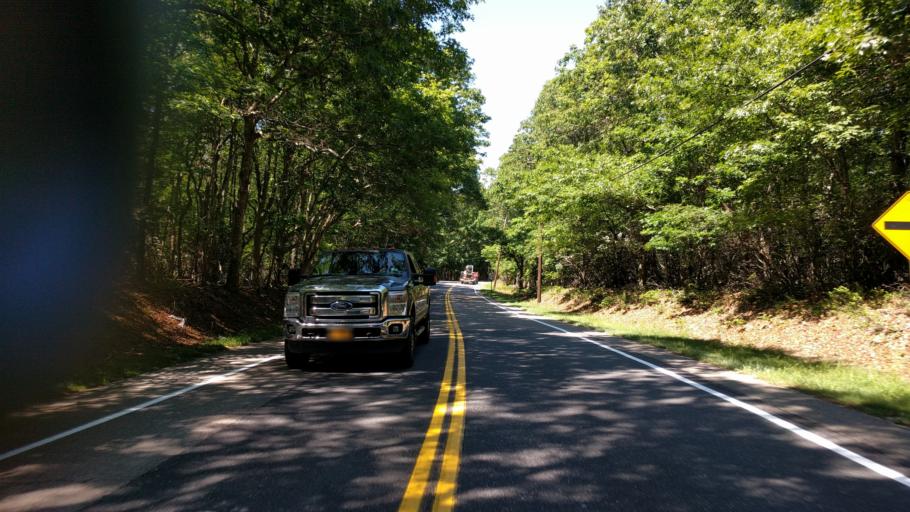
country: US
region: New York
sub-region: Suffolk County
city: Noyack
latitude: 40.9762
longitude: -72.3762
